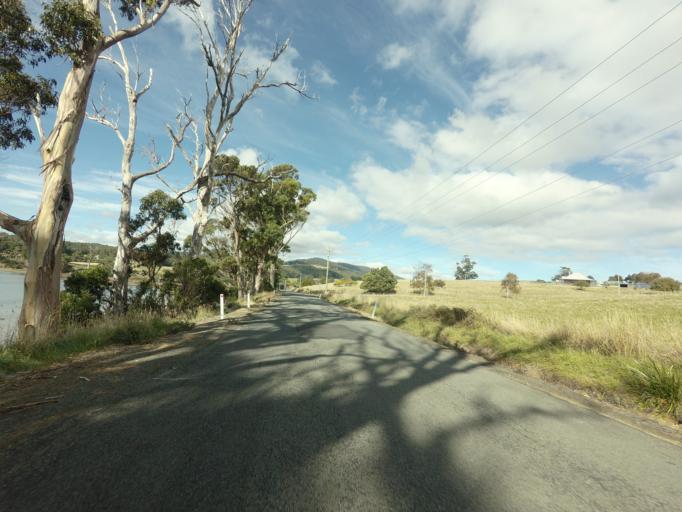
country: AU
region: Tasmania
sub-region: Clarence
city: Sandford
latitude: -43.0525
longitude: 147.7718
